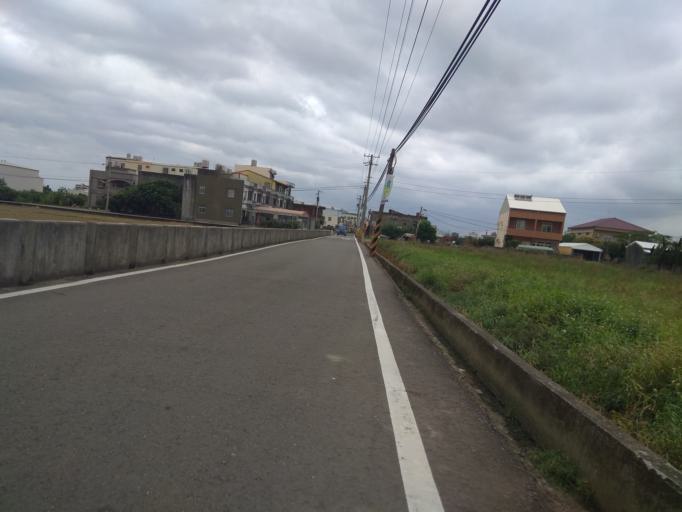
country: TW
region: Taiwan
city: Taoyuan City
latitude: 25.0483
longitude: 121.2198
